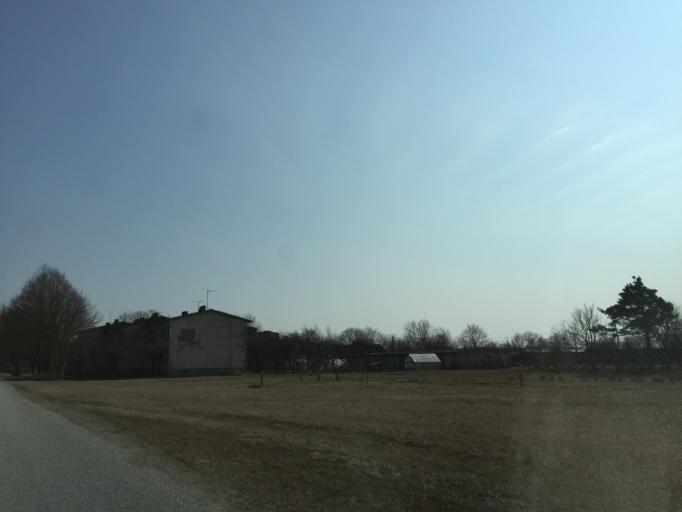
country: EE
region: Saare
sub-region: Kuressaare linn
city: Kuressaare
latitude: 58.3714
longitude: 22.6776
